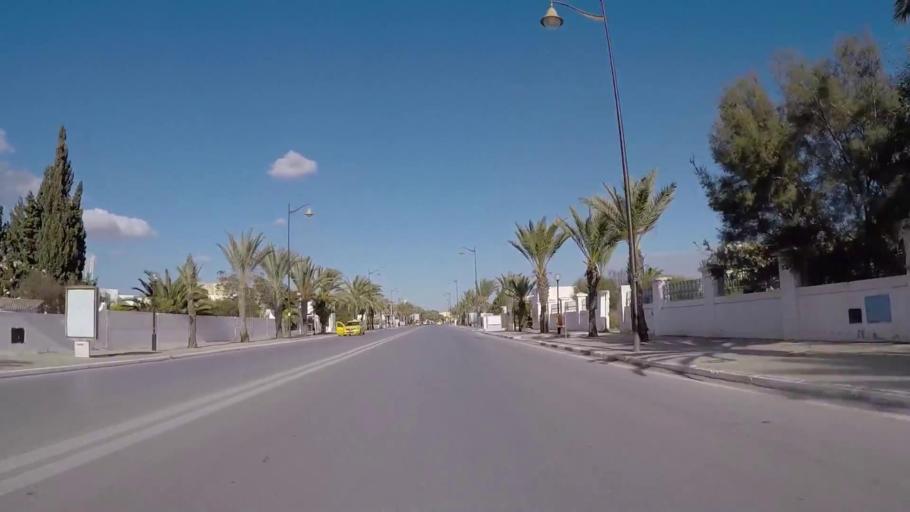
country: TN
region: Nabul
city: Al Hammamat
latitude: 36.3630
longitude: 10.5320
